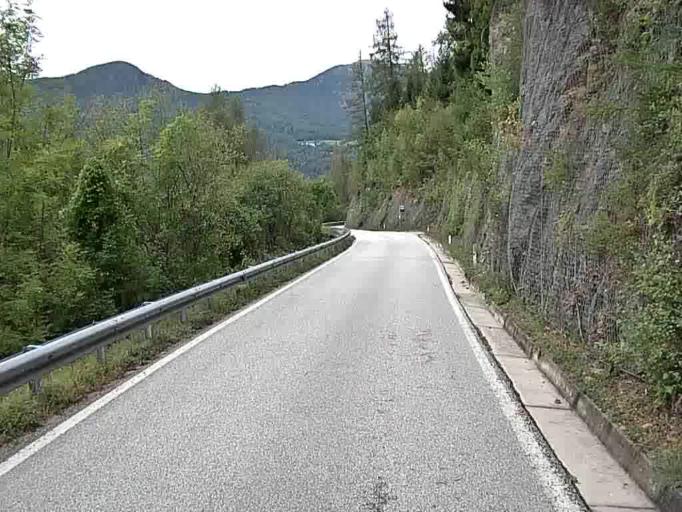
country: IT
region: Trentino-Alto Adige
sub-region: Provincia di Trento
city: Frassilongo
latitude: 46.0735
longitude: 11.2878
